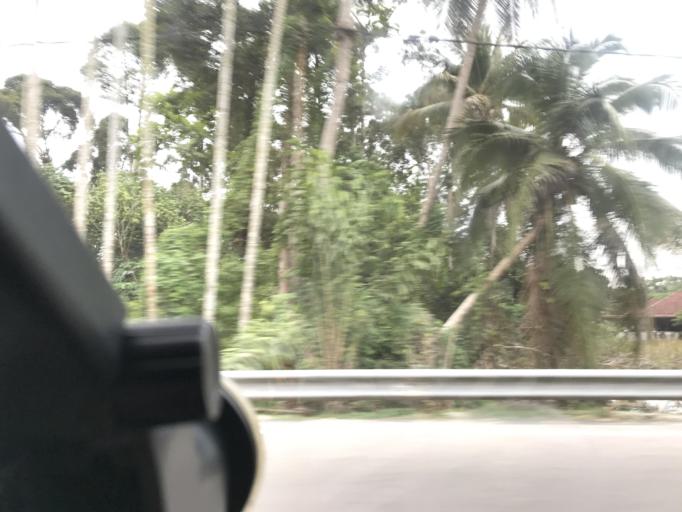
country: MY
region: Kelantan
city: Kota Bharu
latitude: 6.1208
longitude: 102.1763
